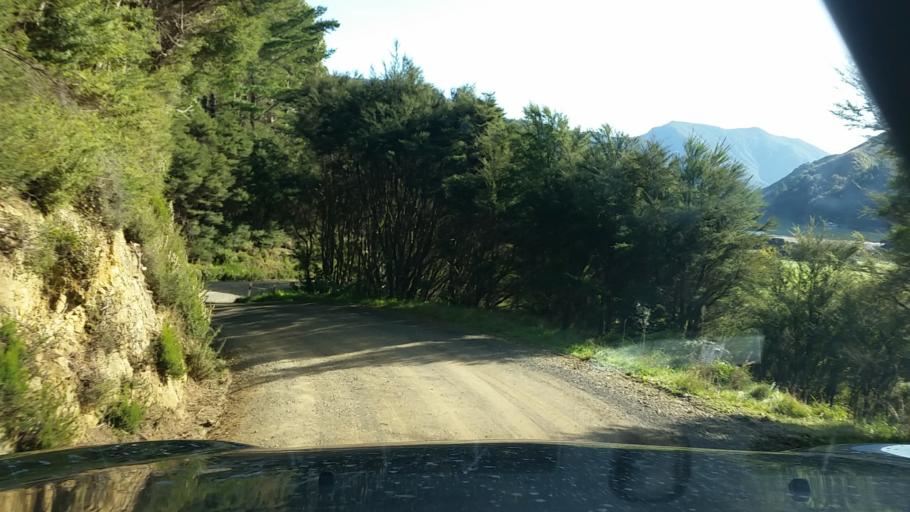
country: NZ
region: Marlborough
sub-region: Marlborough District
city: Picton
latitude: -41.1551
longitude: 173.9693
